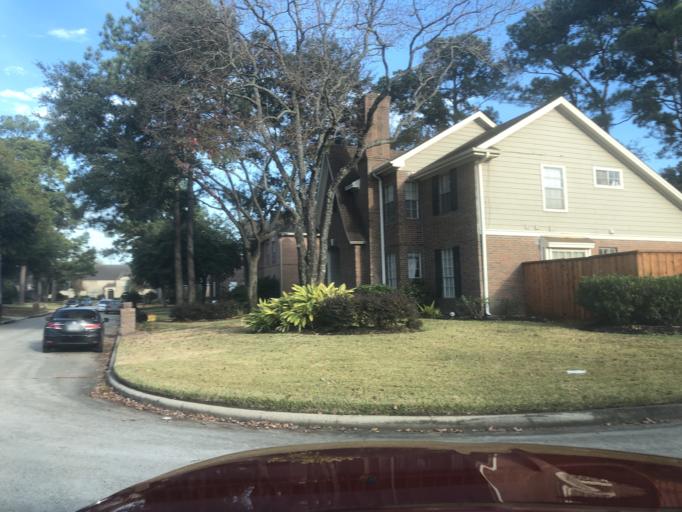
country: US
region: Texas
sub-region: Harris County
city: Spring
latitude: 30.0151
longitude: -95.4680
